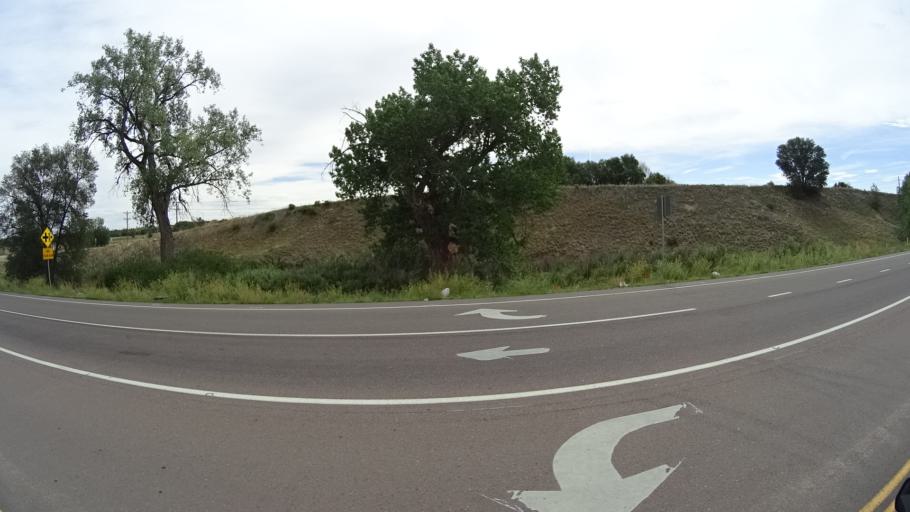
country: US
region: Colorado
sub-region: El Paso County
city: Fountain
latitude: 38.7081
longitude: -104.7115
